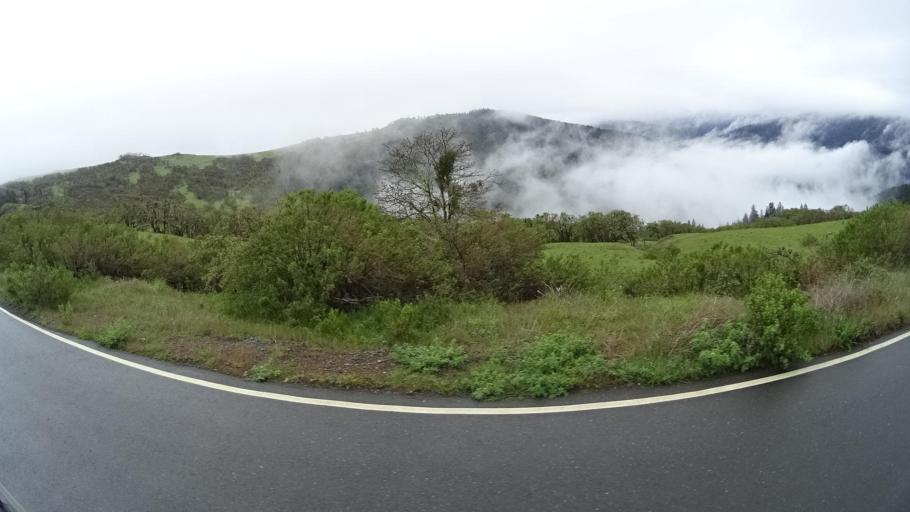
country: US
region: California
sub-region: Humboldt County
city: Westhaven-Moonstone
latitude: 41.1619
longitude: -123.8990
